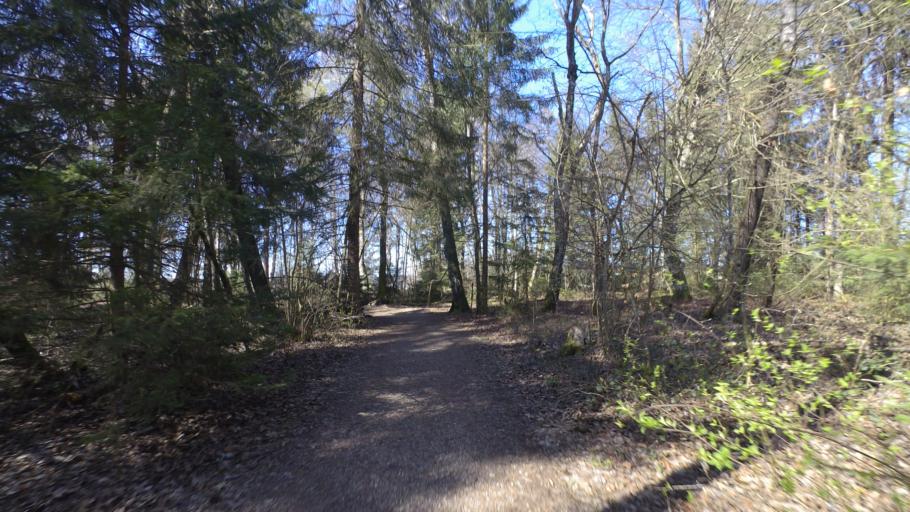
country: DE
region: Bavaria
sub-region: Upper Bavaria
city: Seeon-Seebruck
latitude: 47.9368
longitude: 12.4867
